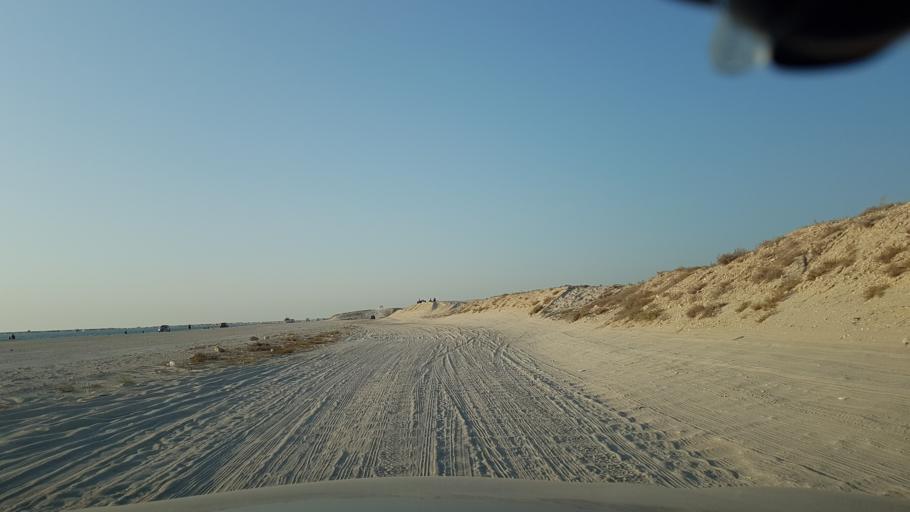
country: BH
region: Manama
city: Jidd Hafs
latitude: 26.2431
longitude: 50.5031
